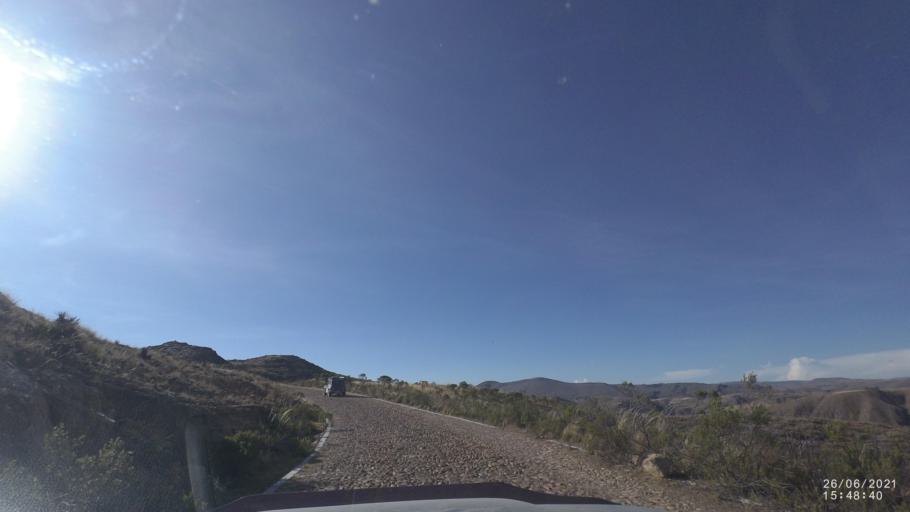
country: BO
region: Cochabamba
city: Arani
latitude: -17.8609
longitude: -65.6954
